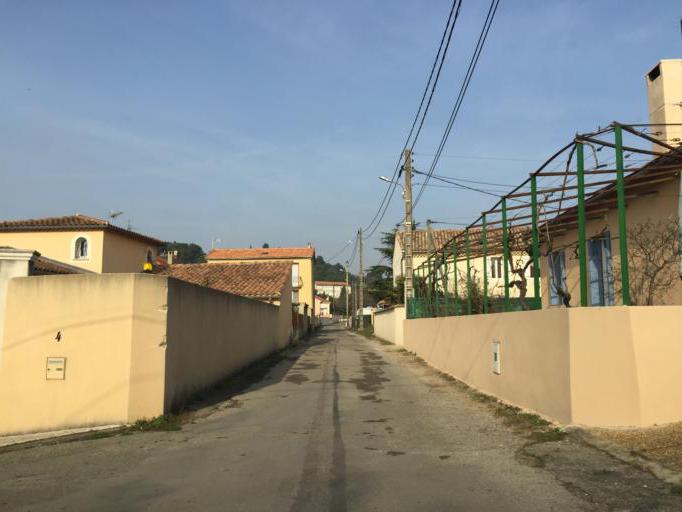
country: FR
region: Provence-Alpes-Cote d'Azur
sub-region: Departement du Vaucluse
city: Orange
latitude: 44.1268
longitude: 4.8136
